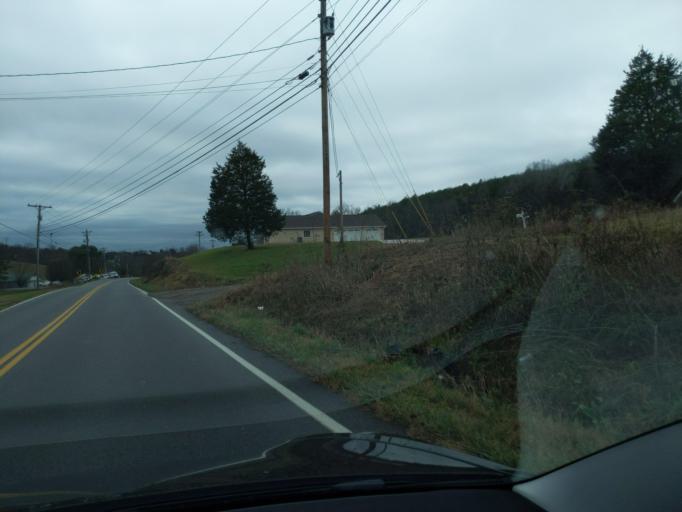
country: US
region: Tennessee
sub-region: Sevier County
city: Sevierville
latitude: 35.9639
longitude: -83.5746
